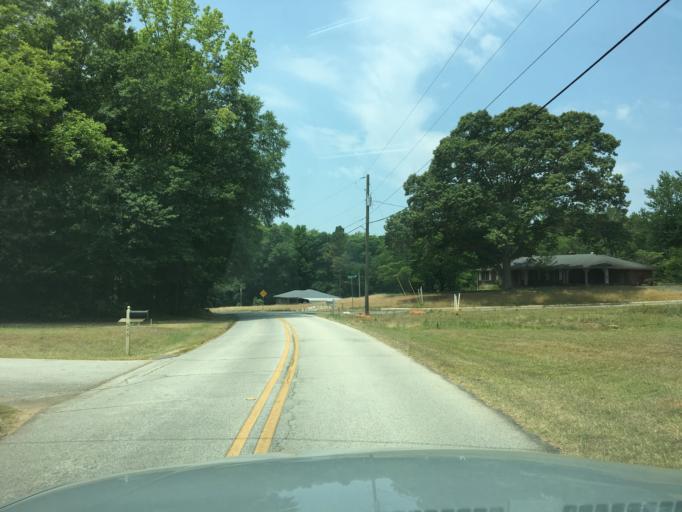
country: US
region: Georgia
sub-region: Hart County
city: Hartwell
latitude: 34.3476
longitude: -82.9091
